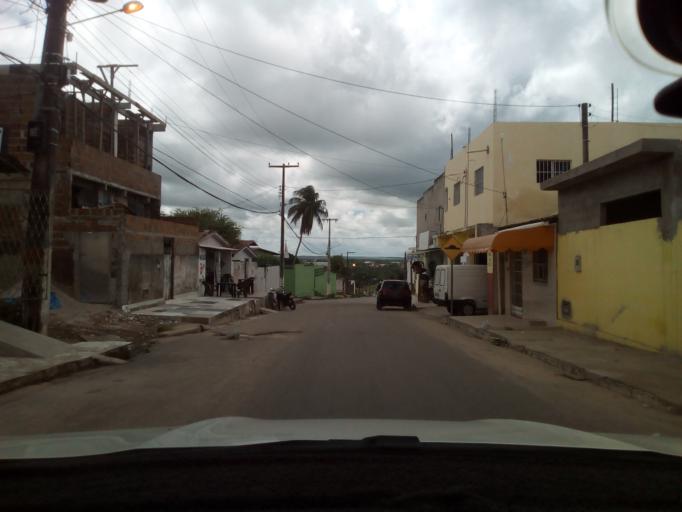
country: BR
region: Paraiba
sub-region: Bayeux
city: Bayeux
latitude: -7.1448
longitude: -34.9230
